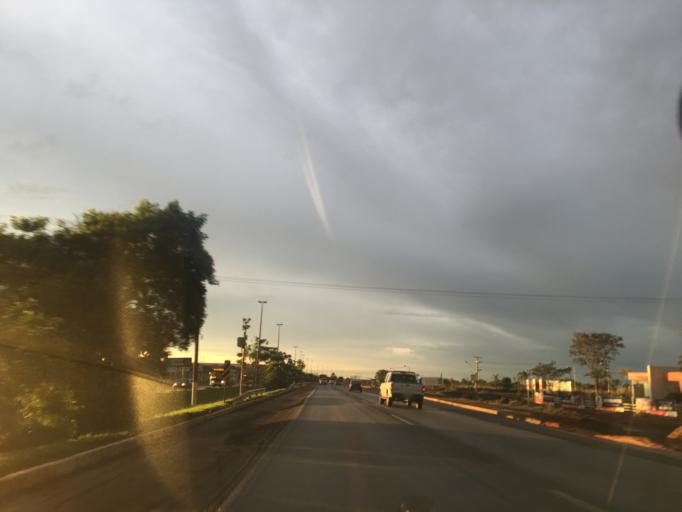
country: BR
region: Goias
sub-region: Luziania
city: Luziania
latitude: -16.0251
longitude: -47.9796
